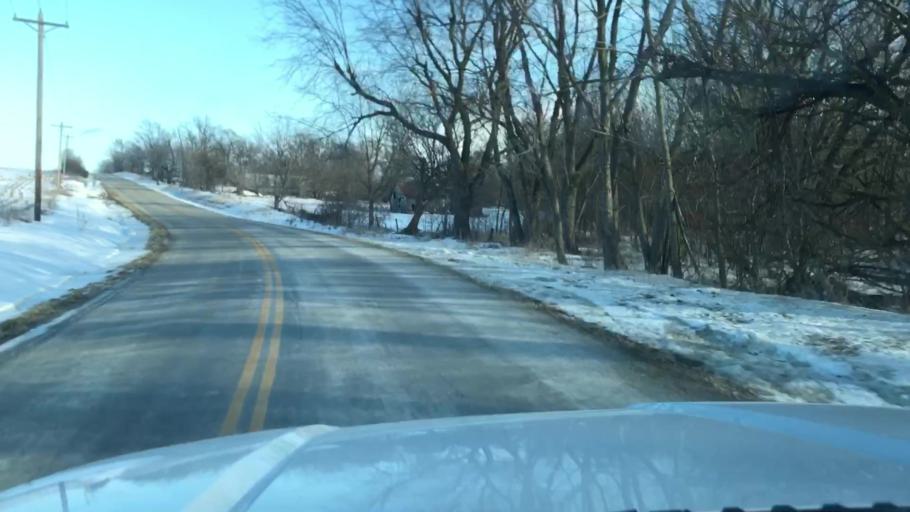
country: US
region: Missouri
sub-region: Holt County
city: Oregon
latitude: 40.1009
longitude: -95.0200
